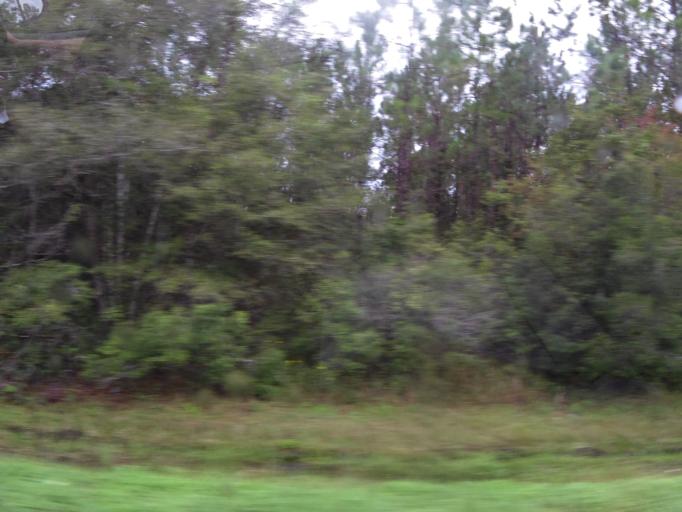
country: US
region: Florida
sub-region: Duval County
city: Baldwin
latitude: 30.4229
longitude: -82.0243
